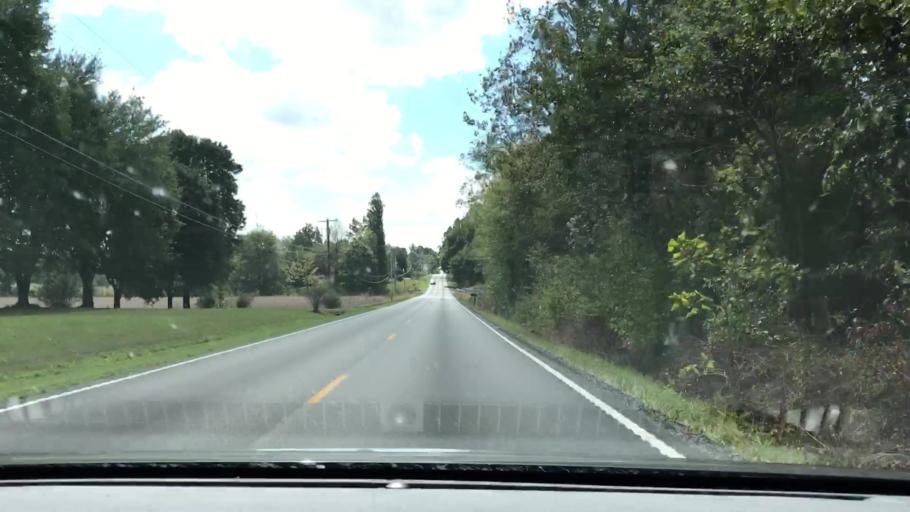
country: US
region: Kentucky
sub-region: Graves County
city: Mayfield
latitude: 36.7867
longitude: -88.5957
